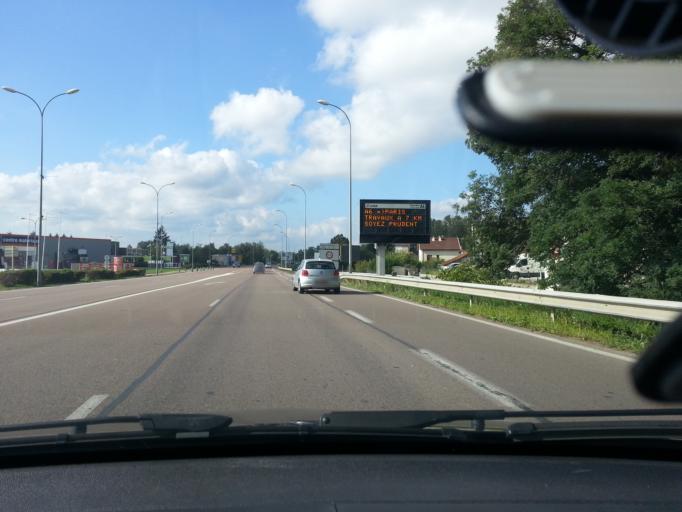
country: FR
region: Bourgogne
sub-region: Departement de Saone-et-Loire
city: Champforgeuil
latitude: 46.7984
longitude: 4.8352
